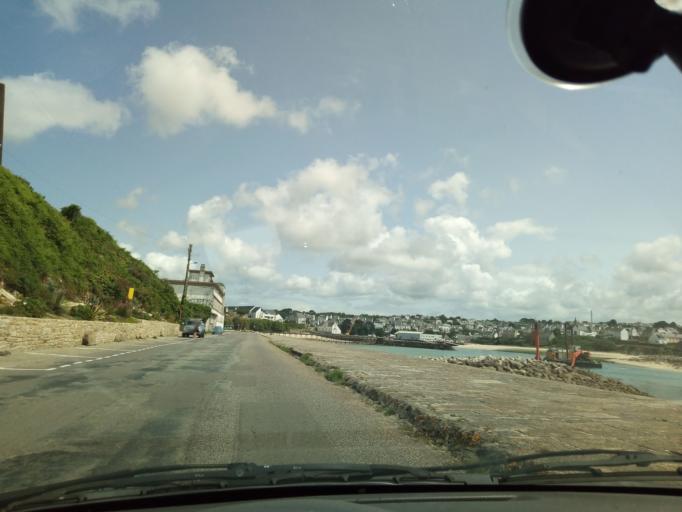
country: FR
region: Brittany
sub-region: Departement du Finistere
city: Audierne
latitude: 48.0144
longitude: -4.5395
